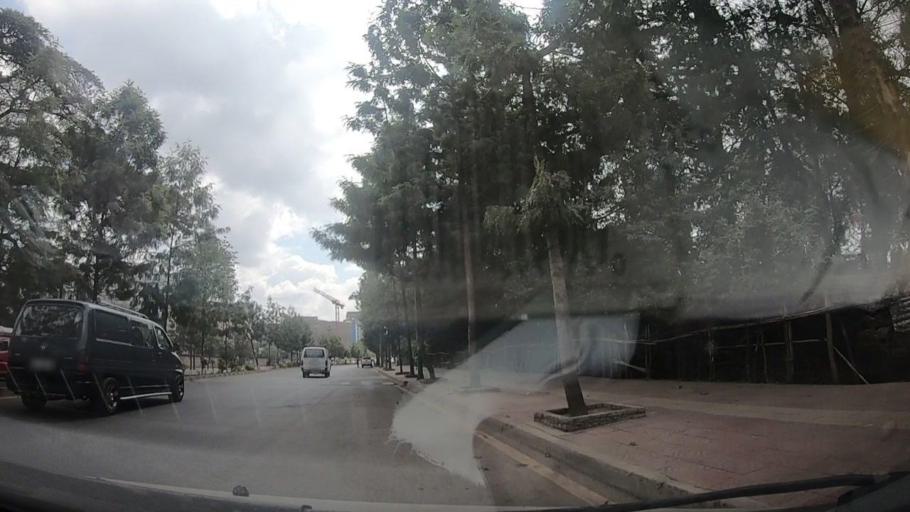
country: ET
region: Adis Abeba
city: Addis Ababa
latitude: 9.0029
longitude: 38.7349
